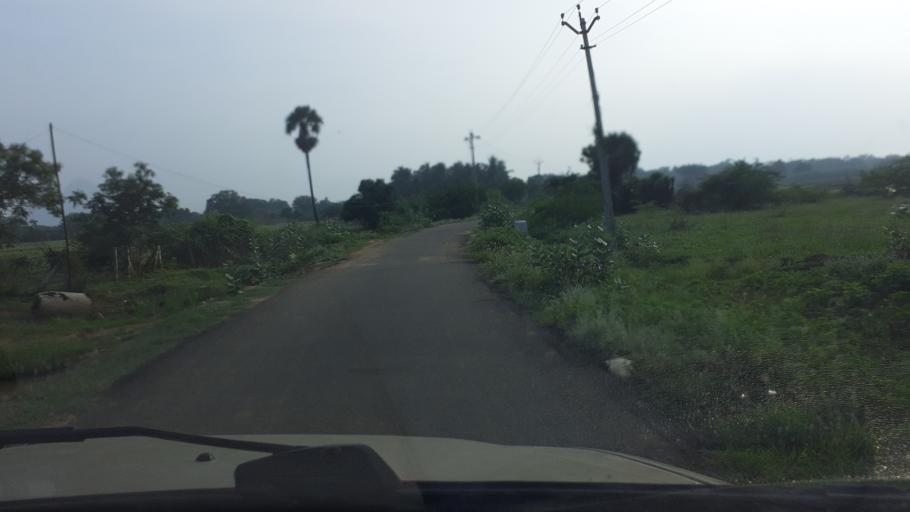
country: IN
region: Tamil Nadu
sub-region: Tirunelveli Kattabo
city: Kalakkadu
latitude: 8.4718
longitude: 77.5861
